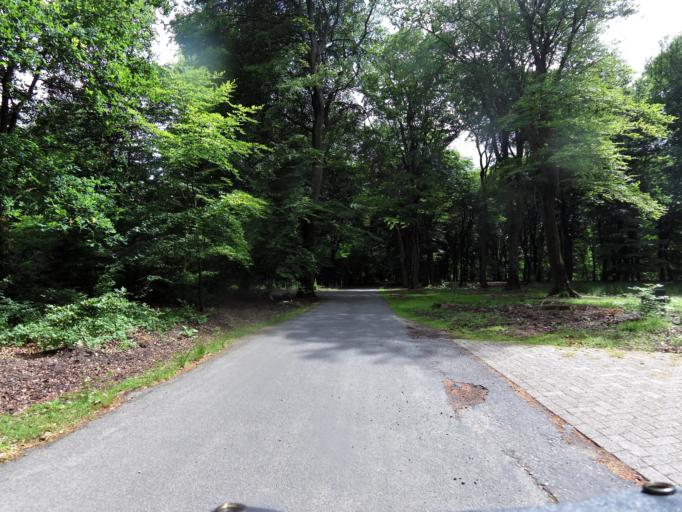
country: NL
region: Gelderland
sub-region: Gemeente Epe
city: Vaassen
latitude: 52.3094
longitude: 5.8799
